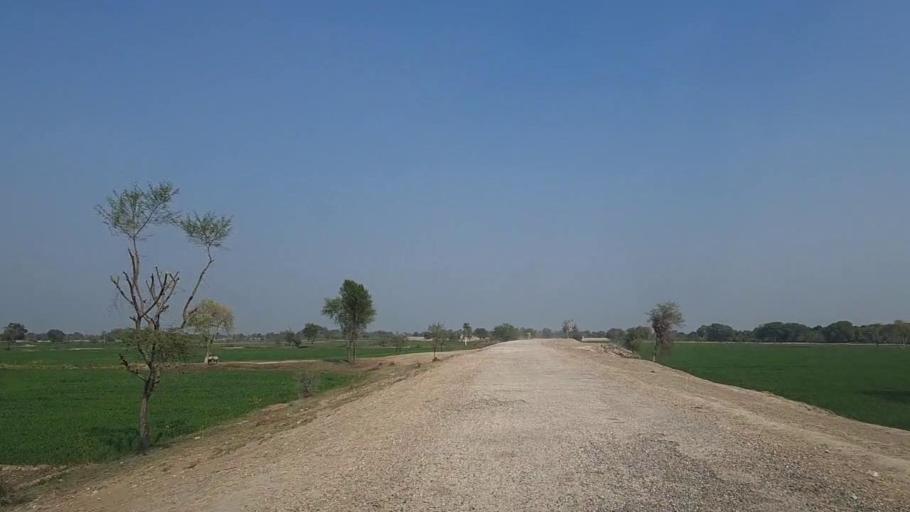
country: PK
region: Sindh
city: Moro
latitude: 26.7977
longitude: 67.9406
